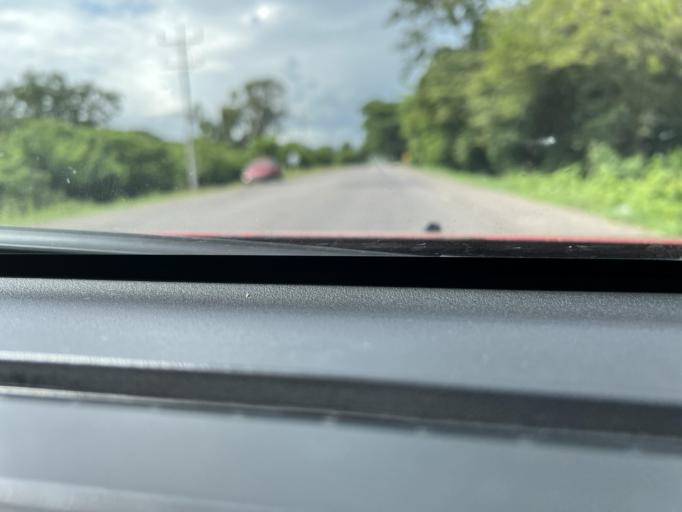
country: SV
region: La Union
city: San Alejo
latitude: 13.3839
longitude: -87.9053
